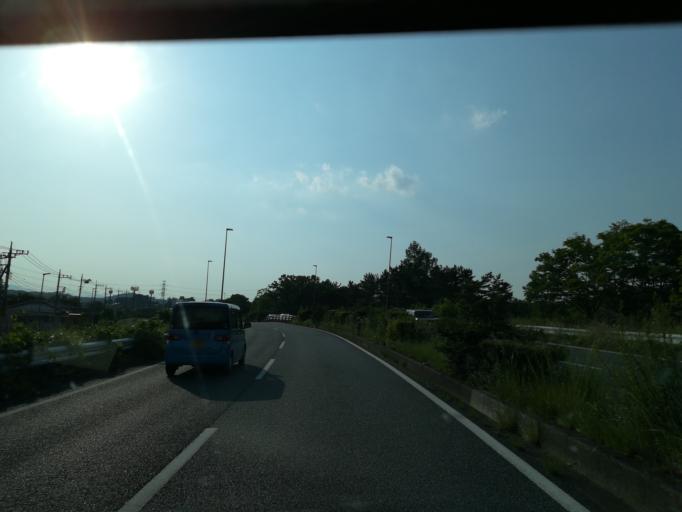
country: JP
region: Saitama
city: Kumagaya
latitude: 36.0662
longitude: 139.3664
